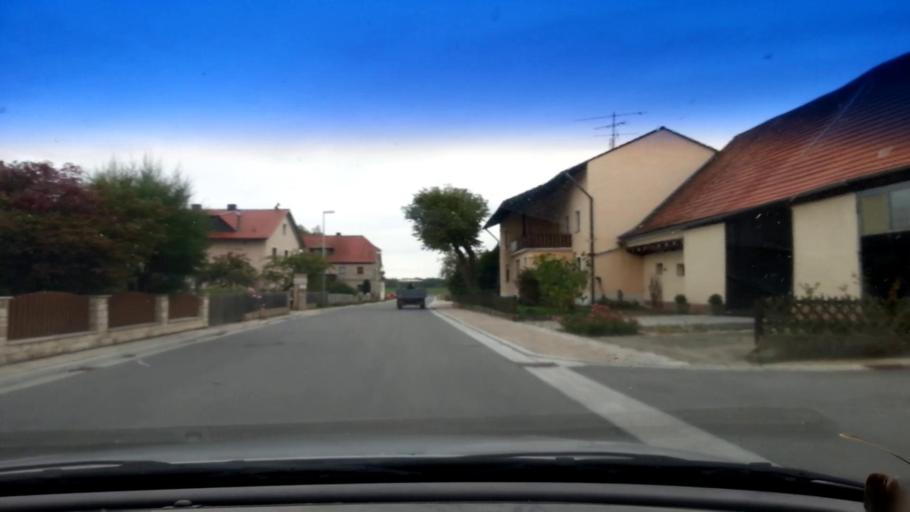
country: DE
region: Bavaria
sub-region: Upper Franconia
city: Priesendorf
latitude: 49.8908
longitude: 10.6527
